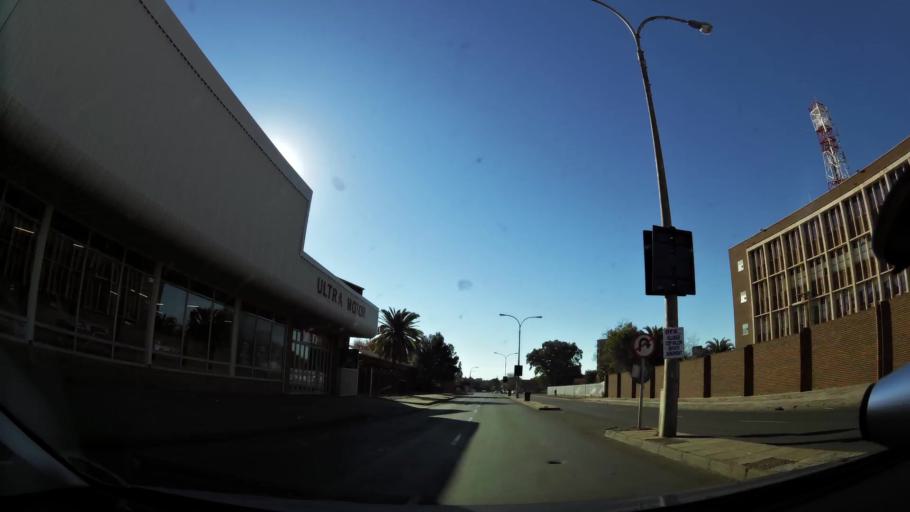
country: ZA
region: Northern Cape
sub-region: Frances Baard District Municipality
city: Kimberley
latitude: -28.7426
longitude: 24.7666
